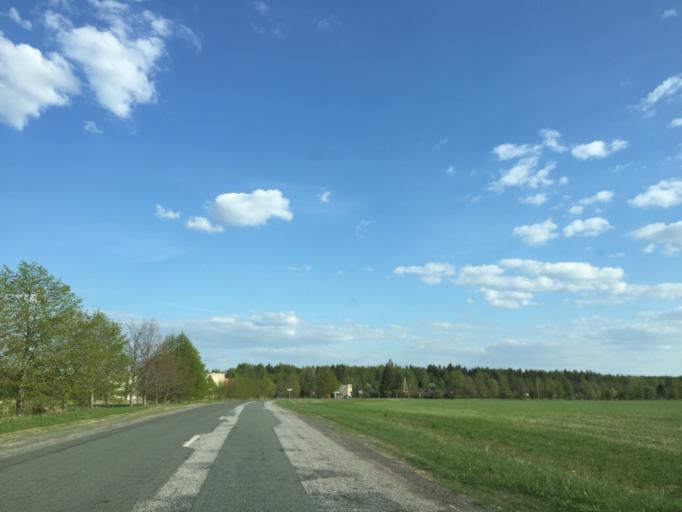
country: LV
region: Sigulda
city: Sigulda
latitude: 57.2569
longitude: 24.8718
